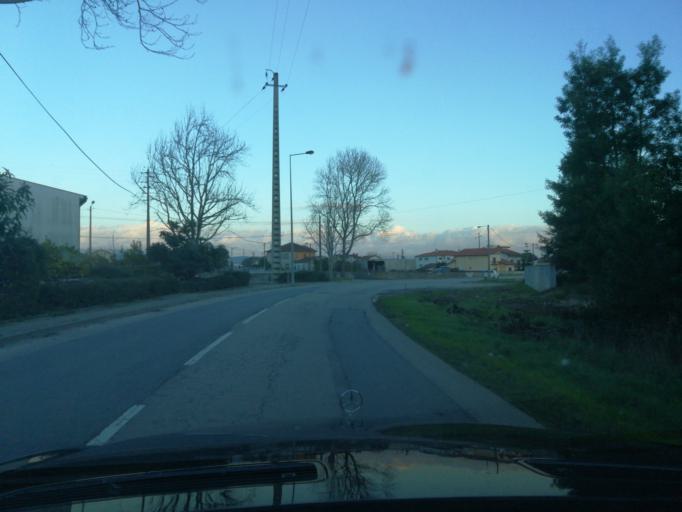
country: PT
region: Aveiro
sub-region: Estarreja
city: Estarreja
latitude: 40.7576
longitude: -8.5889
